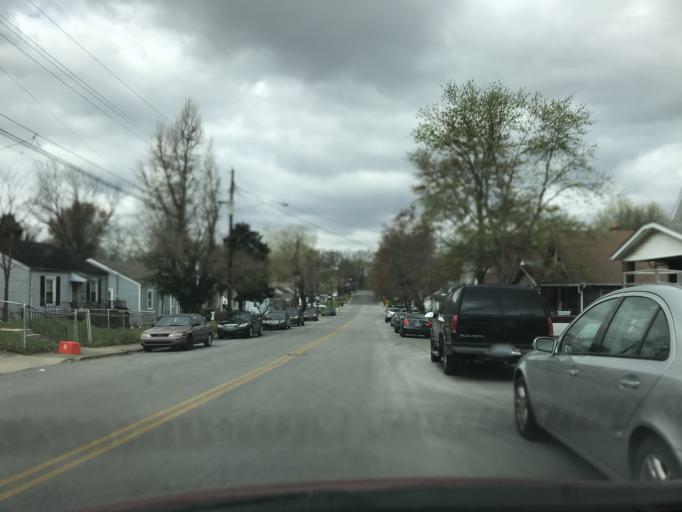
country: US
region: Kentucky
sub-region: Jefferson County
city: Shively
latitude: 38.2419
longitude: -85.8256
